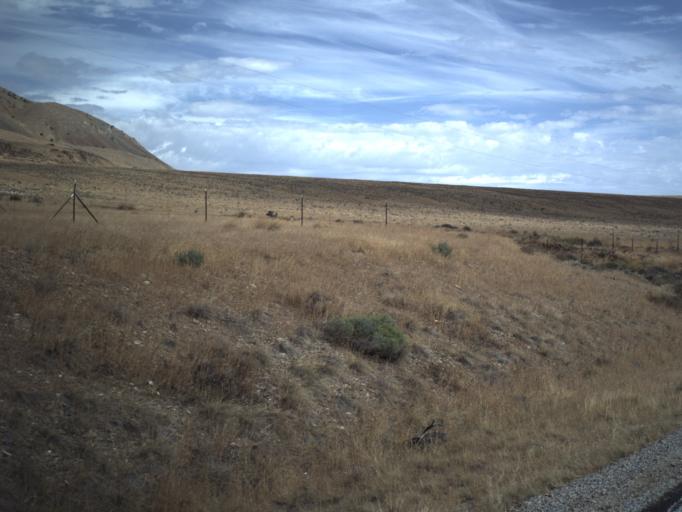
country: US
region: Utah
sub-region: Tooele County
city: Wendover
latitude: 41.4514
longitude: -113.6690
